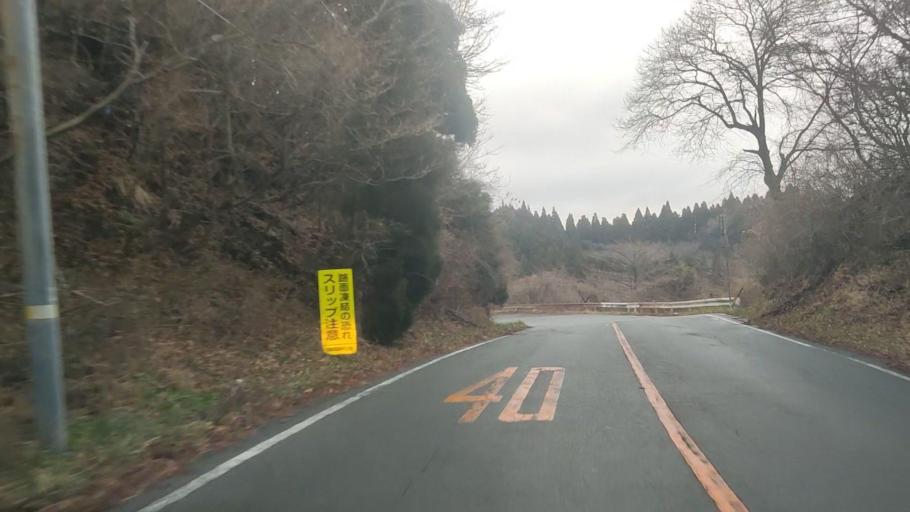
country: JP
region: Kumamoto
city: Aso
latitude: 32.8894
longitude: 131.1688
